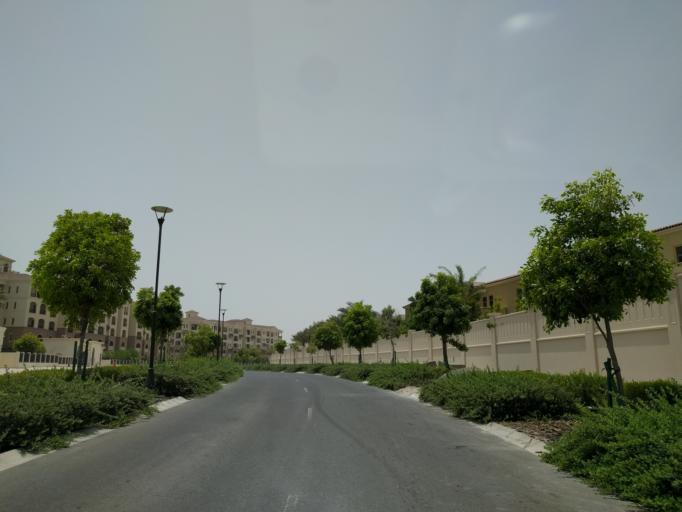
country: AE
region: Abu Dhabi
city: Abu Dhabi
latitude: 24.5521
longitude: 54.4508
